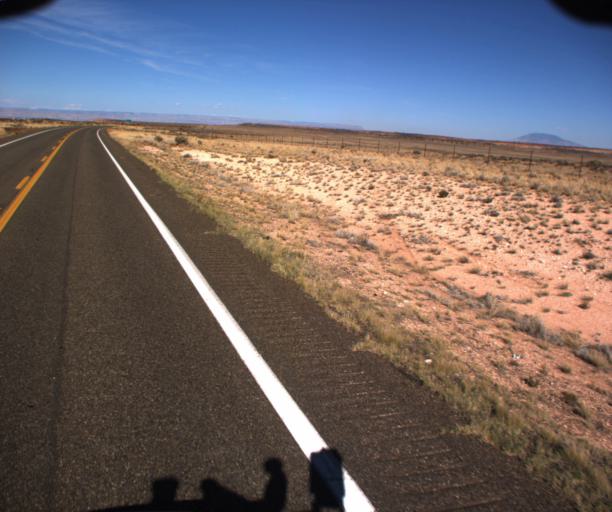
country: US
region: Arizona
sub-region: Coconino County
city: LeChee
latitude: 36.7512
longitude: -111.5744
